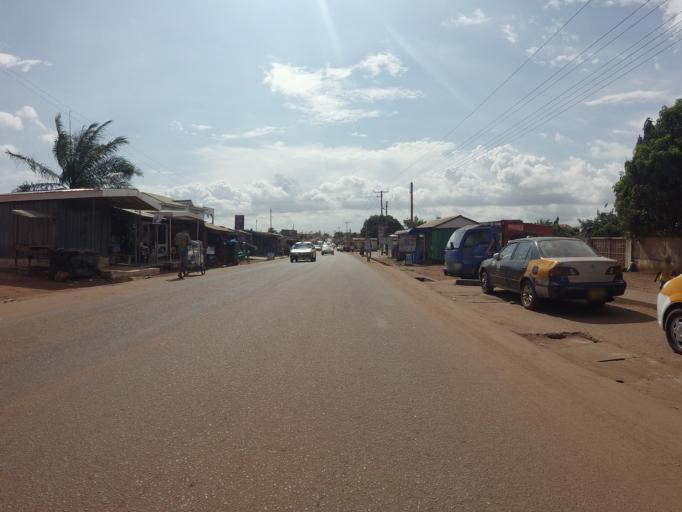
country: GH
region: Greater Accra
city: Medina Estates
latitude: 5.6787
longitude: -0.1752
